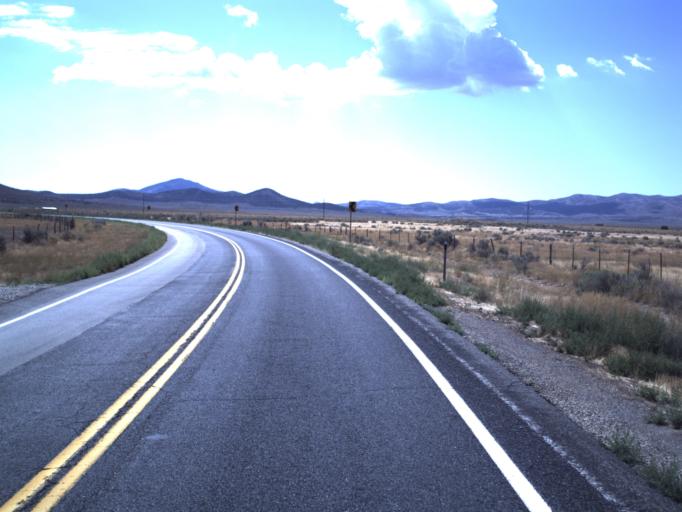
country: US
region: Utah
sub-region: Tooele County
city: Tooele
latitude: 40.0891
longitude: -112.4306
